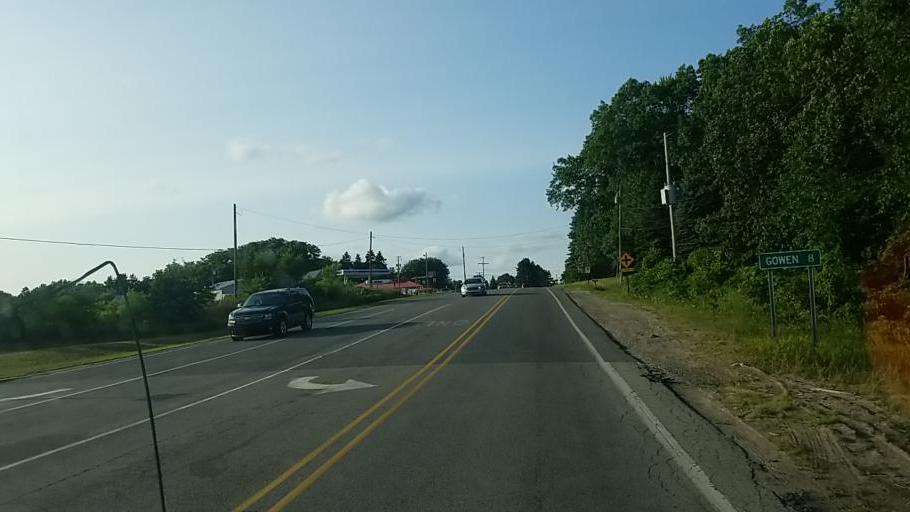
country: US
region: Michigan
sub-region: Montcalm County
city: Greenville
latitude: 43.1749
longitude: -85.3527
